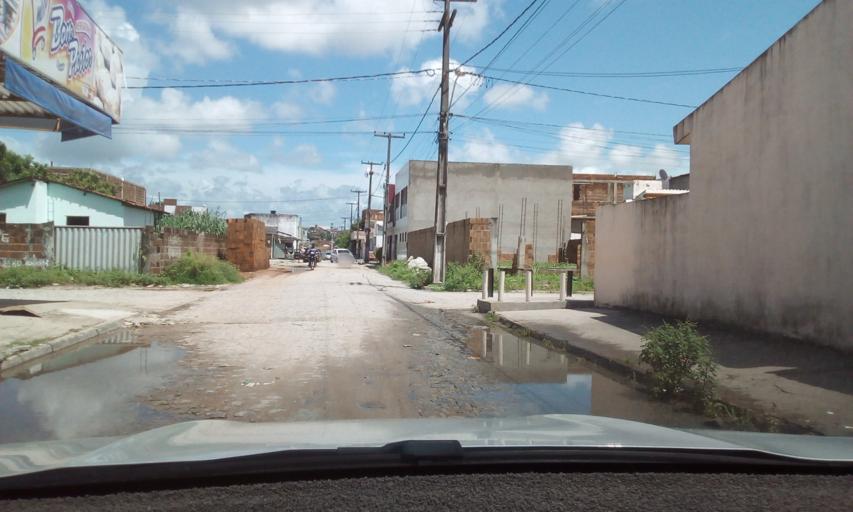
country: BR
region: Paraiba
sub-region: Bayeux
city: Bayeux
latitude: -7.1195
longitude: -34.9375
